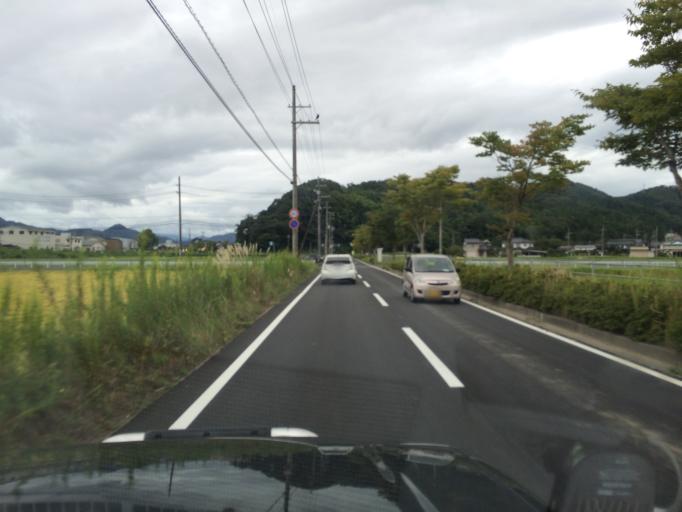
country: JP
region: Hyogo
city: Toyooka
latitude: 35.5103
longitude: 134.8134
